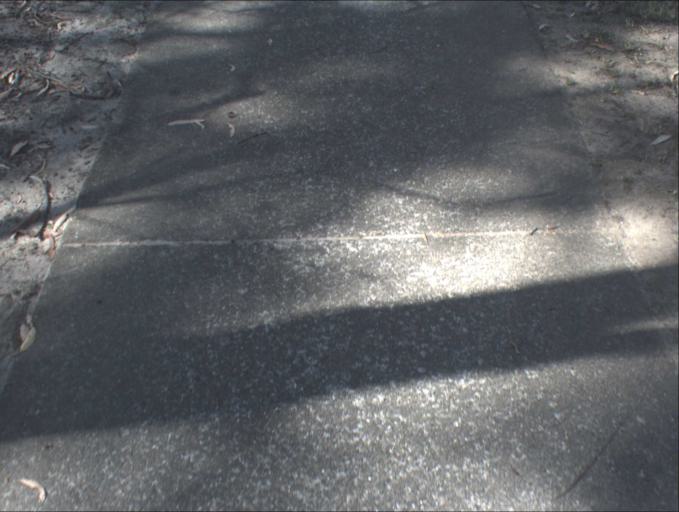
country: AU
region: Queensland
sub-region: Logan
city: Slacks Creek
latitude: -27.6424
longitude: 153.1872
